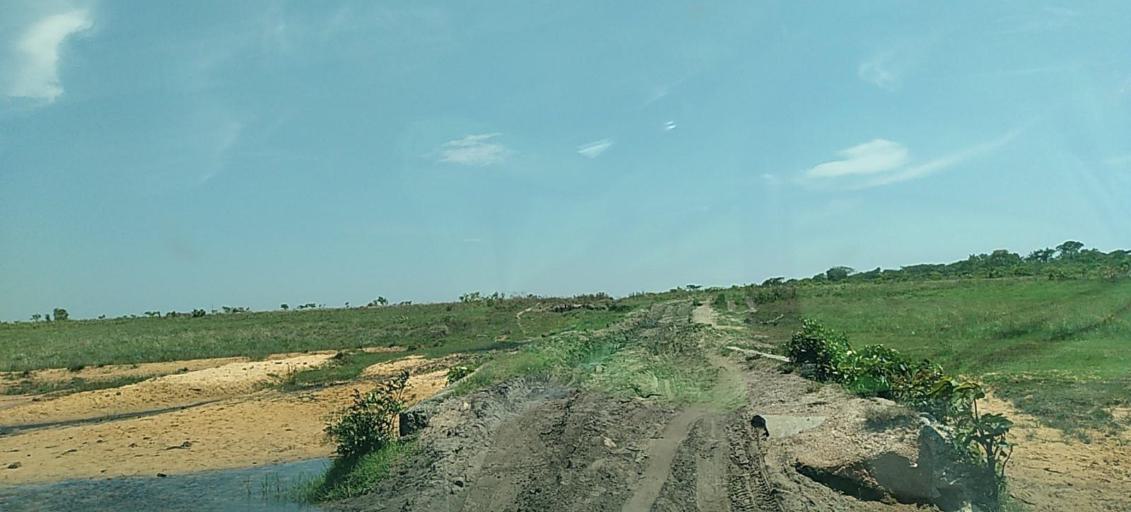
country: ZM
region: North-Western
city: Mwinilunga
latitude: -11.6657
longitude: 25.2040
